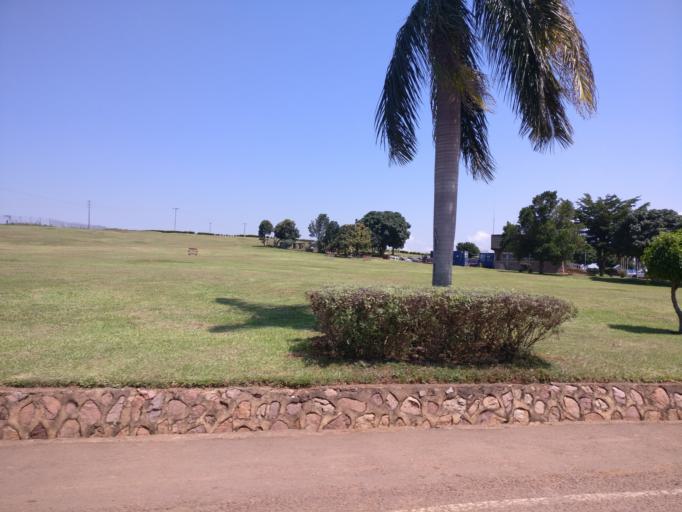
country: UG
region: Central Region
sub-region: Wakiso District
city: Entebbe
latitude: 0.0429
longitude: 32.4476
